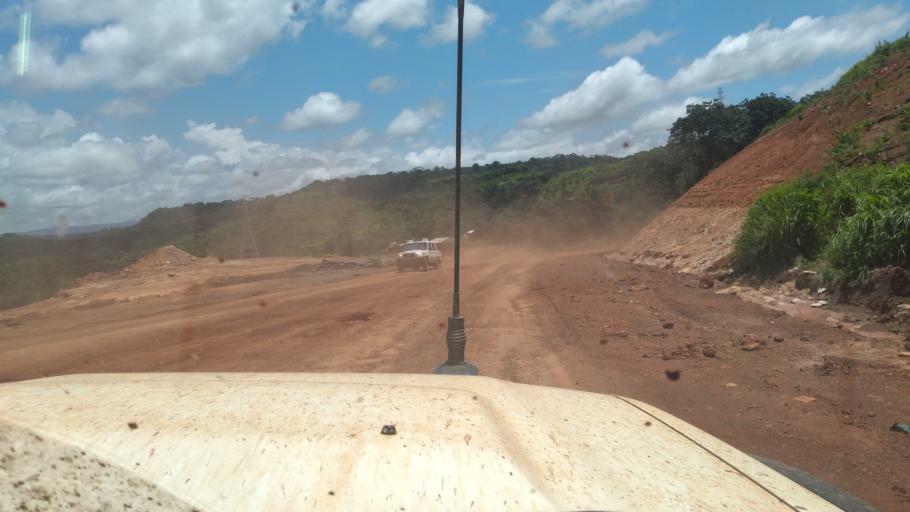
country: GN
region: Kindia
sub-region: Kindia
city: Kindia
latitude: 10.1782
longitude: -12.4717
